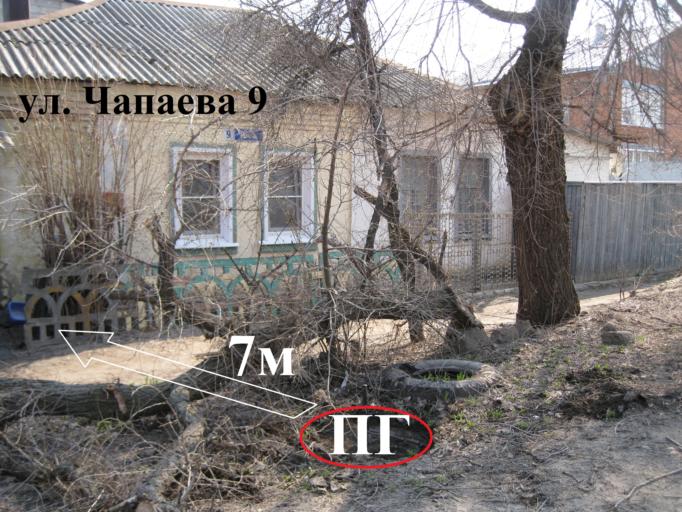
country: RU
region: Voronezj
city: Voronezh
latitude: 51.6442
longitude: 39.1852
